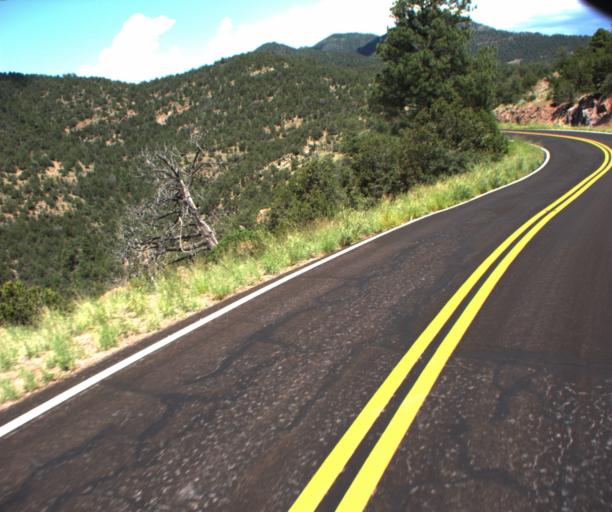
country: US
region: Arizona
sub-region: Greenlee County
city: Morenci
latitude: 33.4021
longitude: -109.3488
